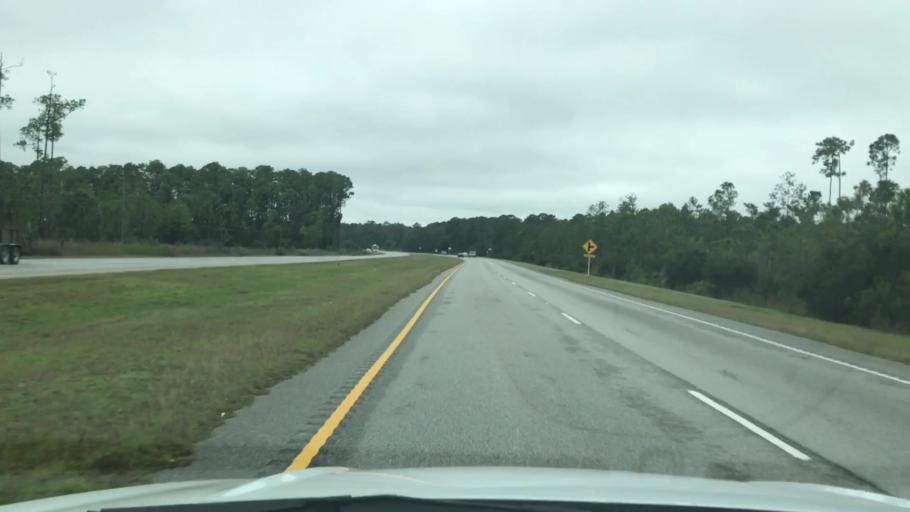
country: US
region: South Carolina
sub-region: Beaufort County
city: Laurel Bay
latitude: 32.3739
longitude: -80.8419
